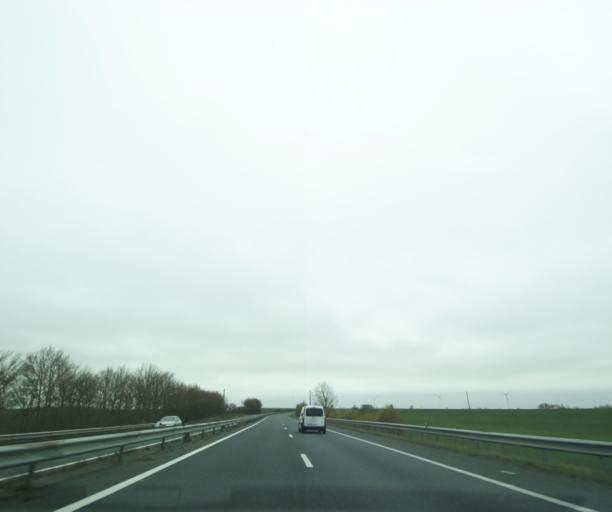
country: FR
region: Centre
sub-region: Departement de l'Indre
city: Vatan
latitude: 47.0641
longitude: 1.8201
